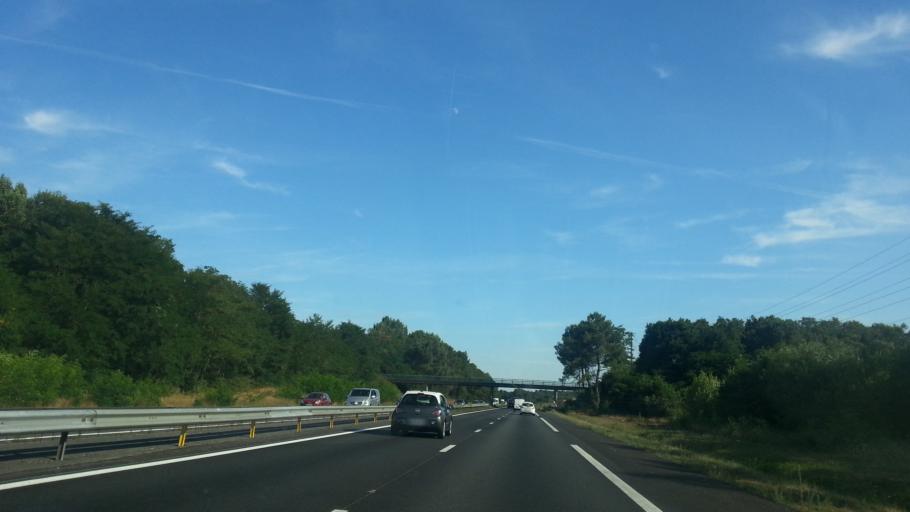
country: FR
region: Aquitaine
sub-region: Departement de la Gironde
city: Martillac
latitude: 44.7203
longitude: -0.5224
